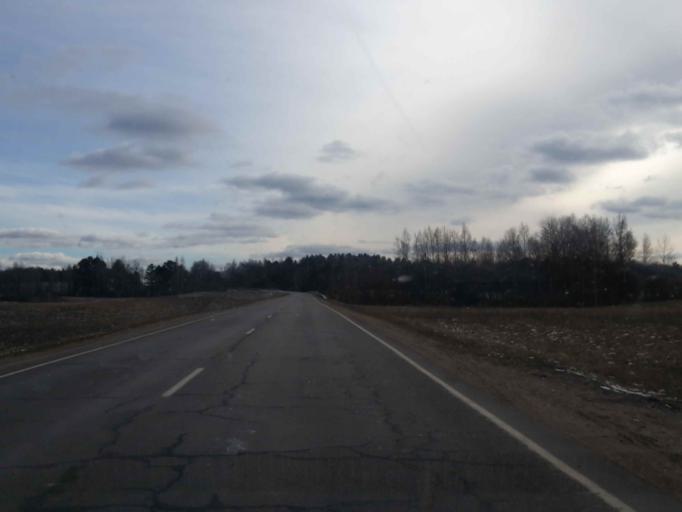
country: BY
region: Minsk
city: Myadzyel
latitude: 54.9077
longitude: 26.9028
